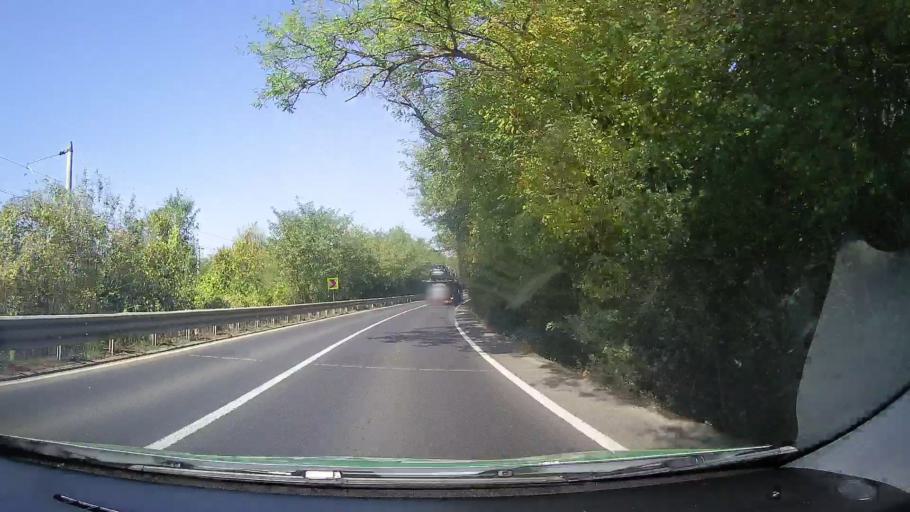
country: RO
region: Arad
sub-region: Comuna Bata
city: Bata
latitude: 46.0388
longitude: 22.0598
